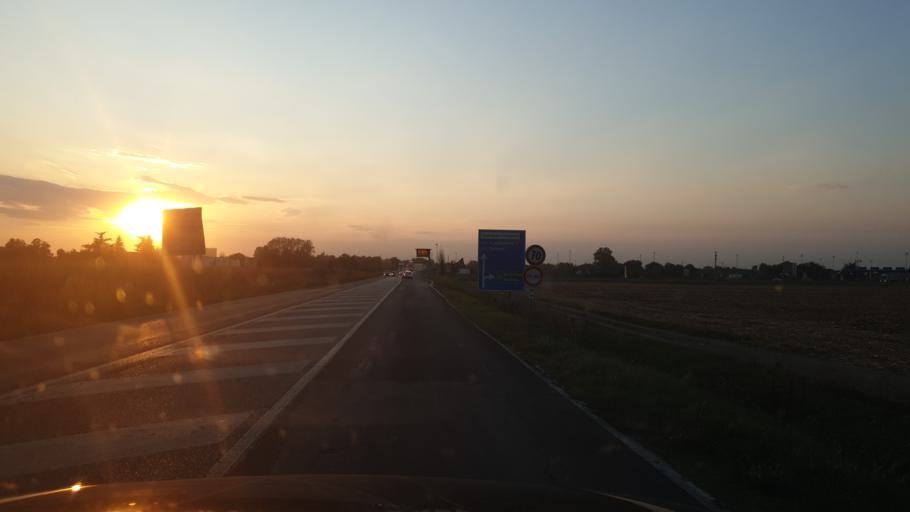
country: IT
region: Emilia-Romagna
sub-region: Provincia di Bologna
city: Progresso
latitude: 44.5852
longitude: 11.4046
